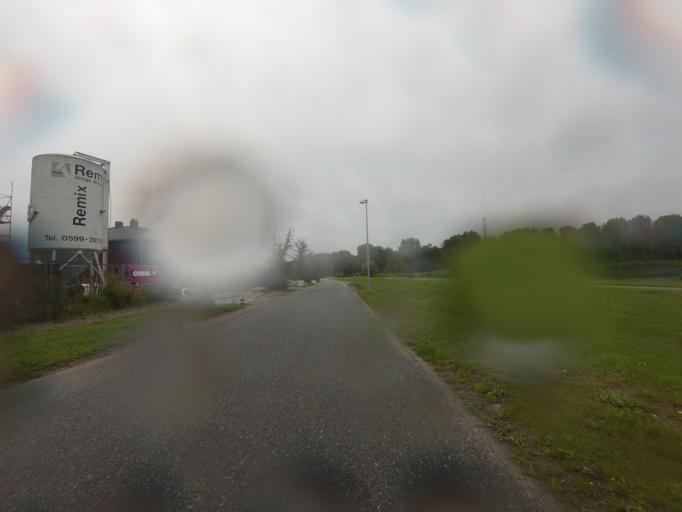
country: NL
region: North Holland
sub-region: Gemeente Huizen
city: Huizen
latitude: 52.3316
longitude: 5.2618
